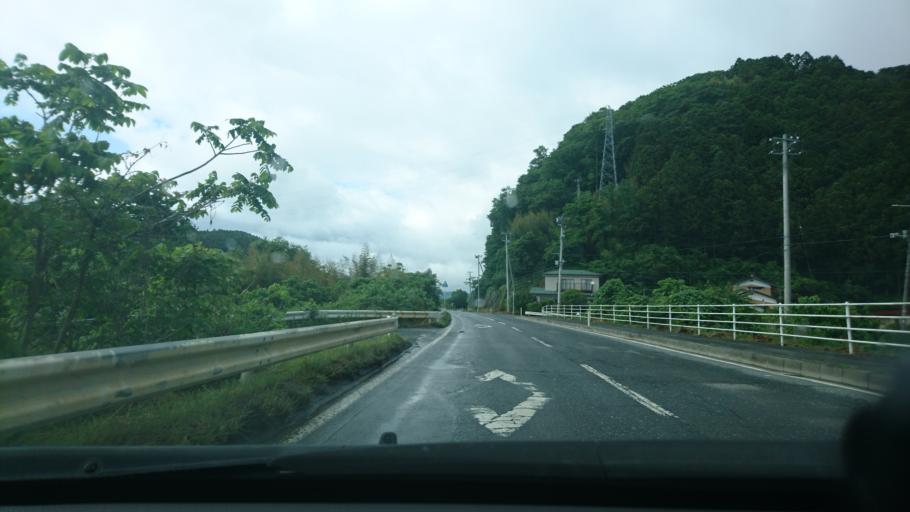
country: JP
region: Miyagi
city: Ishinomaki
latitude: 38.5771
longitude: 141.3017
